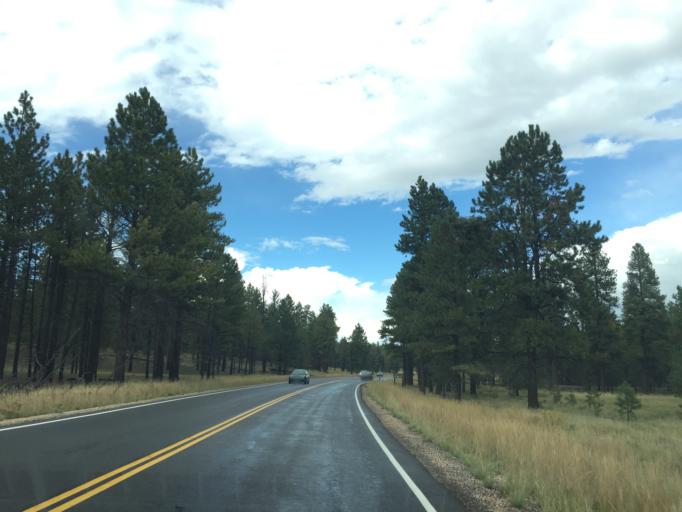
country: US
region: Utah
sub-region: Garfield County
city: Panguitch
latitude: 37.6328
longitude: -112.1736
